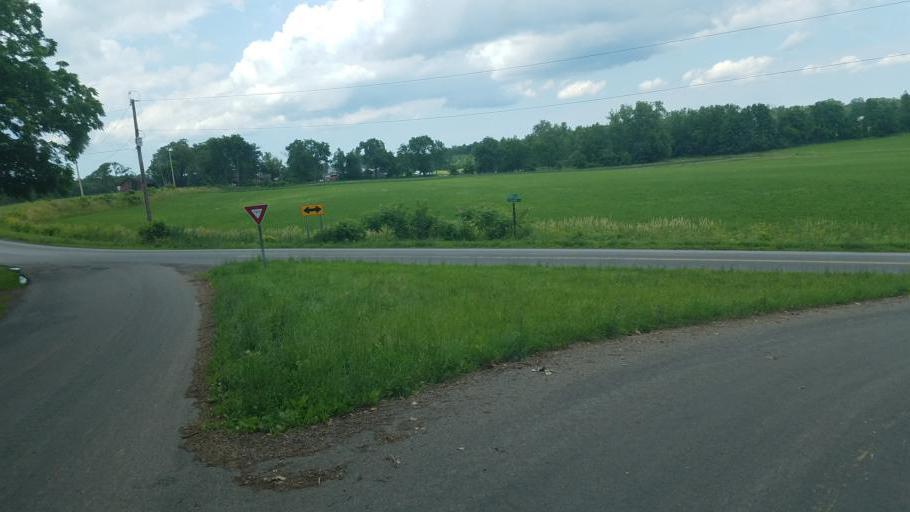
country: US
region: New York
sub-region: Wayne County
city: Clyde
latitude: 43.0151
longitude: -76.8772
